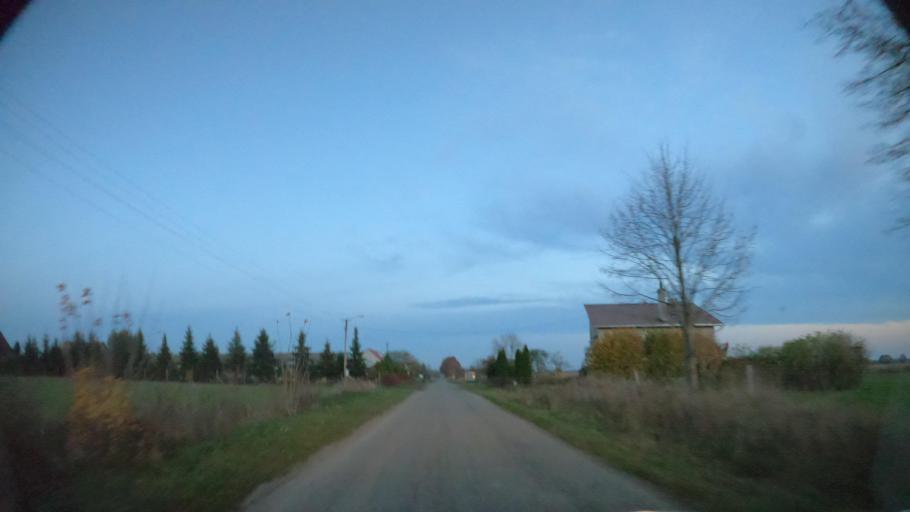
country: PL
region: Greater Poland Voivodeship
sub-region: Powiat zlotowski
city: Sypniewo
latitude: 53.4263
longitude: 16.6193
